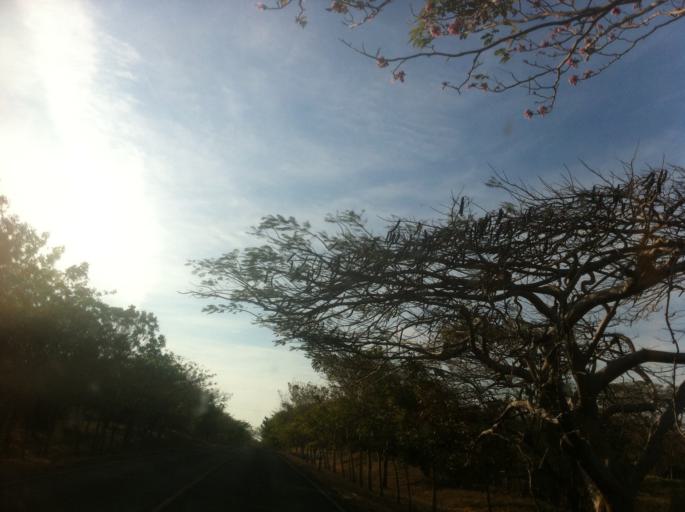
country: NI
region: Rivas
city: San Jorge
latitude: 11.3213
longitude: -85.7128
